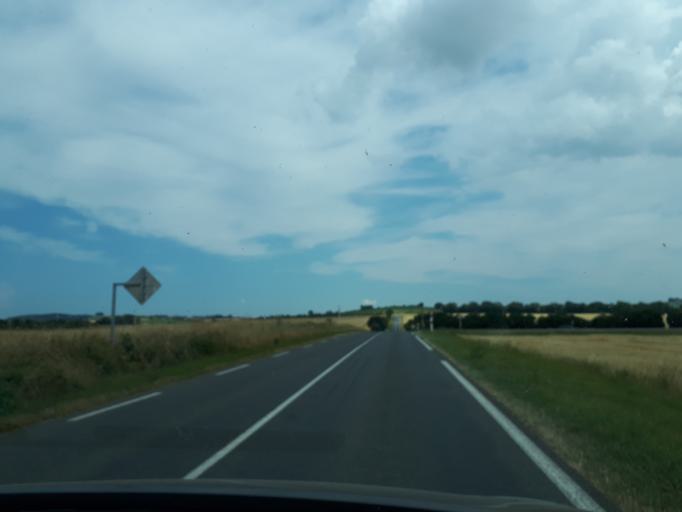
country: FR
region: Centre
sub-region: Departement du Cher
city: Rians
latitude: 47.2275
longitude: 2.6374
